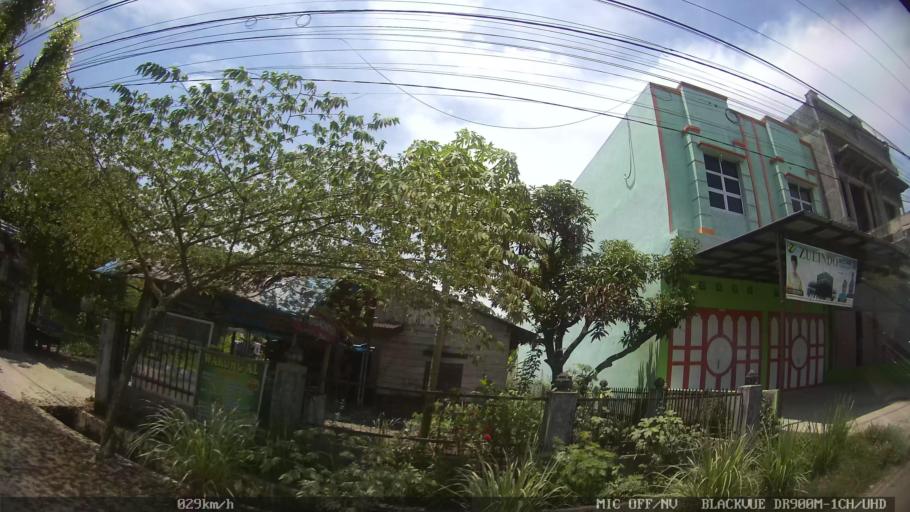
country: ID
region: North Sumatra
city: Binjai
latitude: 3.5912
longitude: 98.5051
